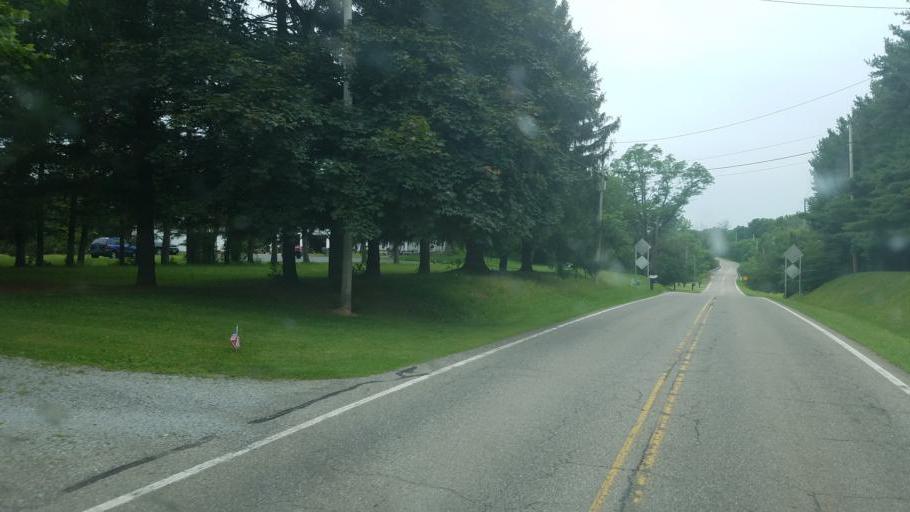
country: US
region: Ohio
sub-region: Trumbull County
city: Cortland
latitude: 41.2993
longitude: -80.7552
